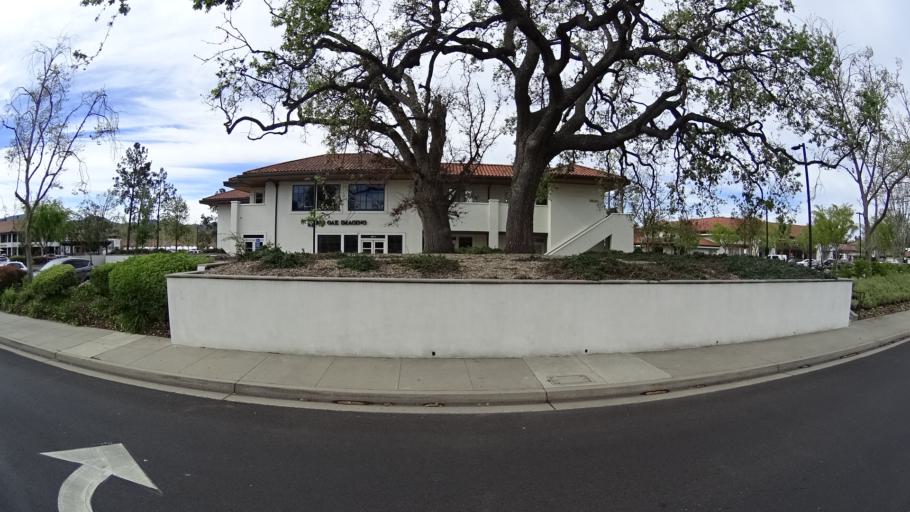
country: US
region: California
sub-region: Los Angeles County
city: Westlake Village
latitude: 34.1529
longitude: -118.8241
